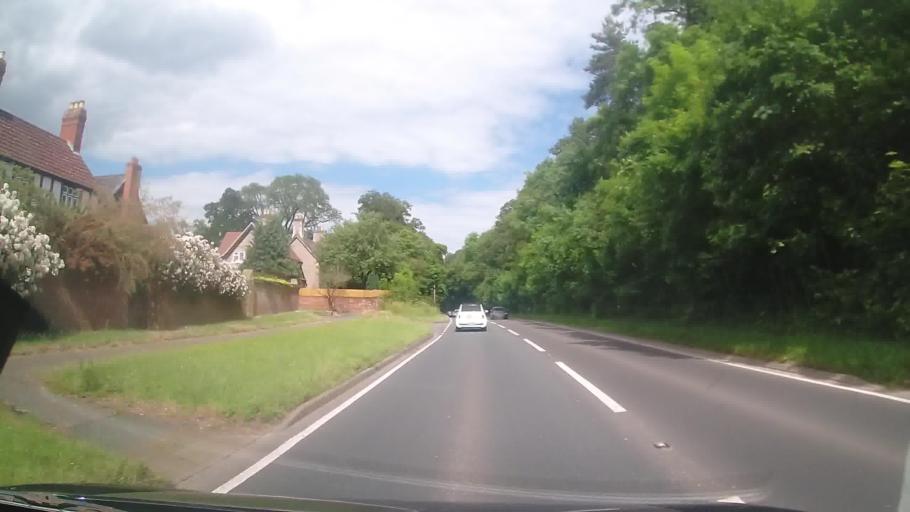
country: GB
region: England
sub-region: Herefordshire
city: Belmont
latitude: 52.0371
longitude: -2.7563
